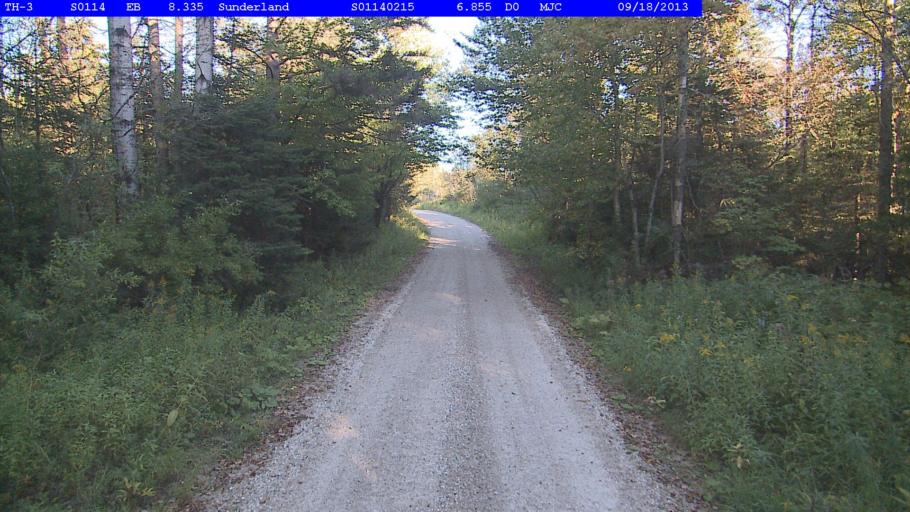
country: US
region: Vermont
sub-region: Bennington County
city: Arlington
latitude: 43.0524
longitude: -73.0520
